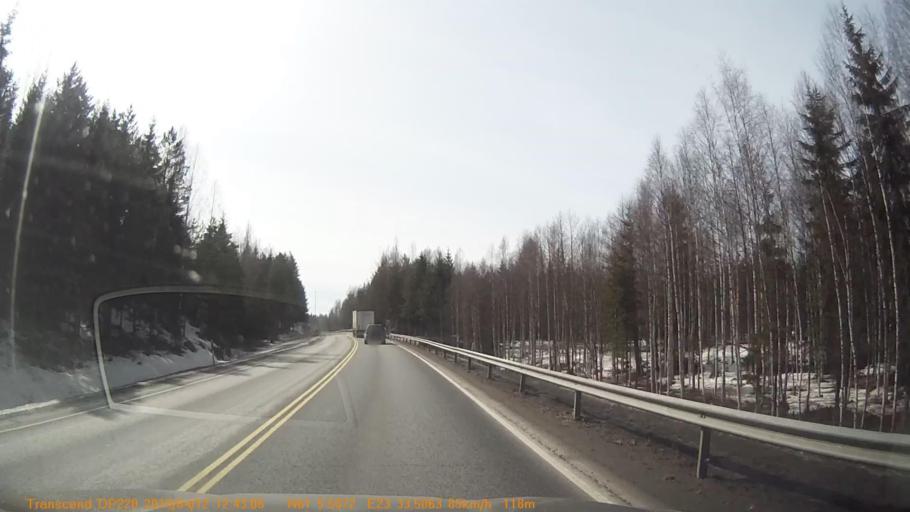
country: FI
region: Pirkanmaa
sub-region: Etelae-Pirkanmaa
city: Urjala
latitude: 61.0917
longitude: 23.5582
